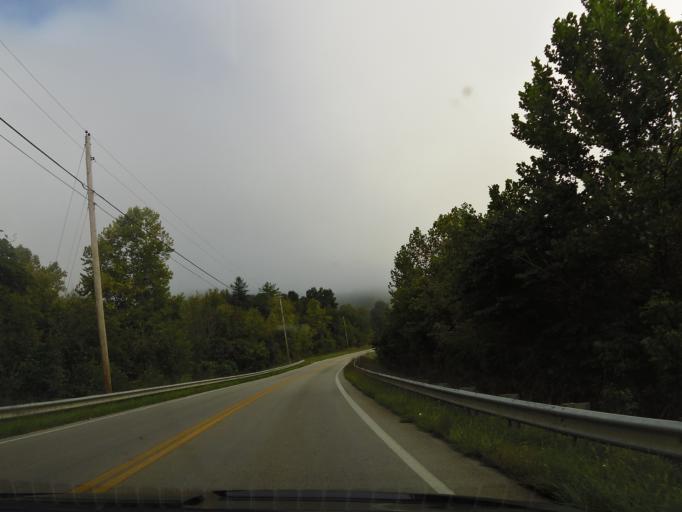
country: US
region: Kentucky
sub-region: Whitley County
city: Williamsburg
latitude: 36.6889
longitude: -84.1416
